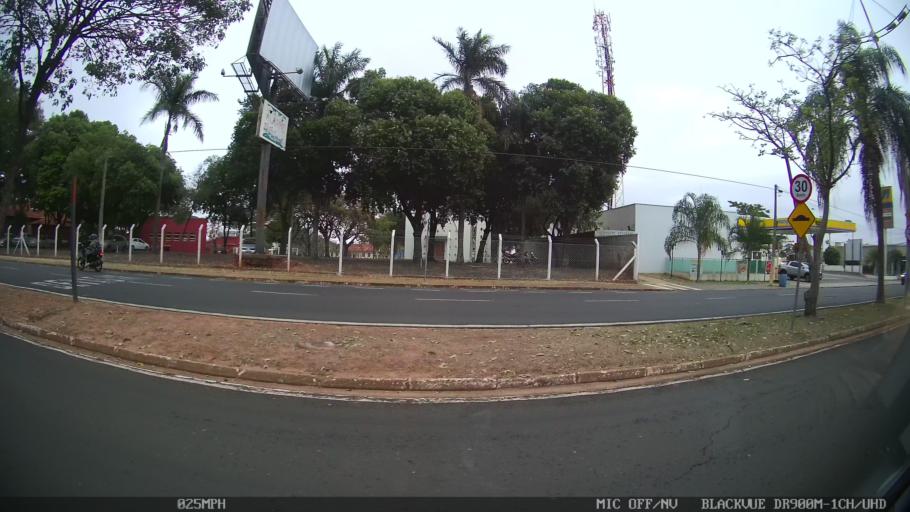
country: BR
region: Sao Paulo
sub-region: Sao Jose Do Rio Preto
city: Sao Jose do Rio Preto
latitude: -20.8366
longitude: -49.4007
